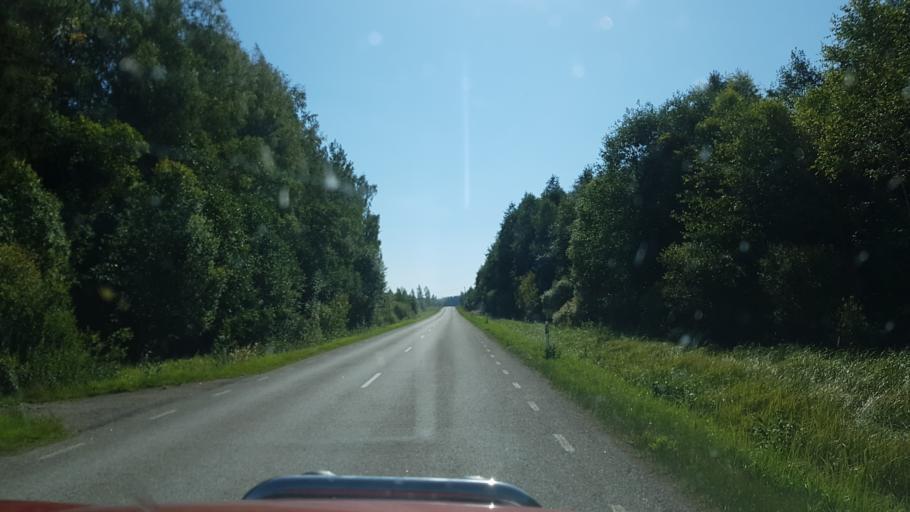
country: EE
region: Polvamaa
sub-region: Polva linn
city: Polva
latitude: 58.2315
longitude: 27.2217
